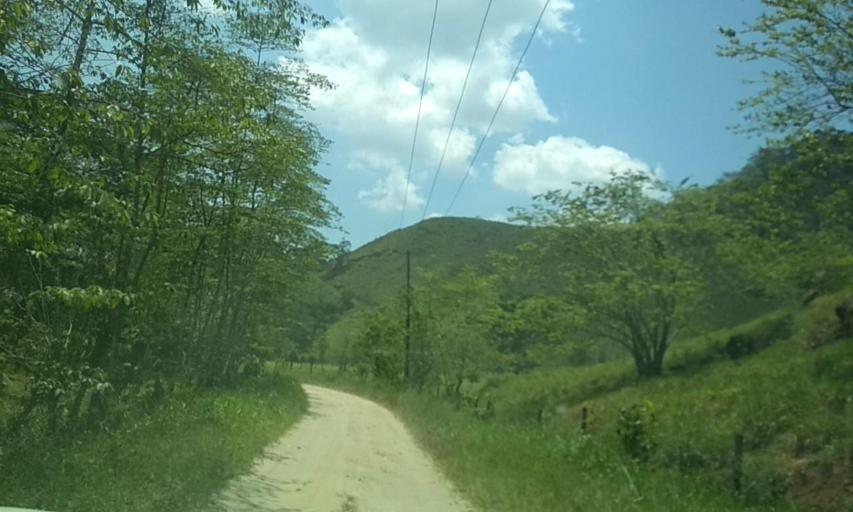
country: MX
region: Chiapas
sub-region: Tecpatan
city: Raudales Malpaso
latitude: 17.2816
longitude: -93.8249
